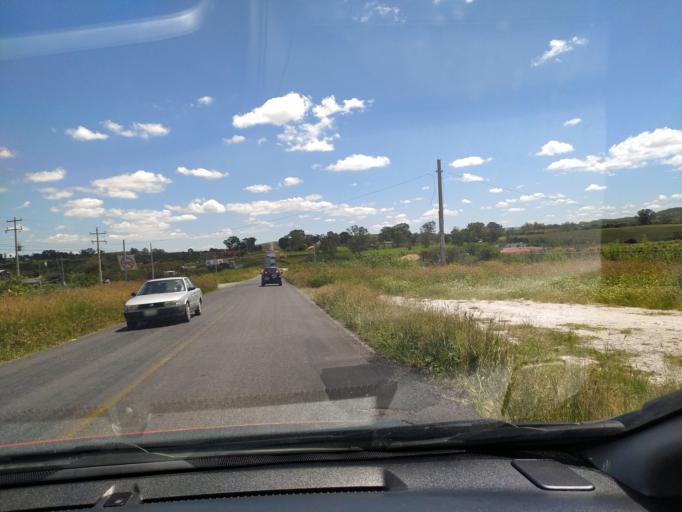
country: MX
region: Jalisco
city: San Diego de Alejandria
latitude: 21.0059
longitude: -102.0532
